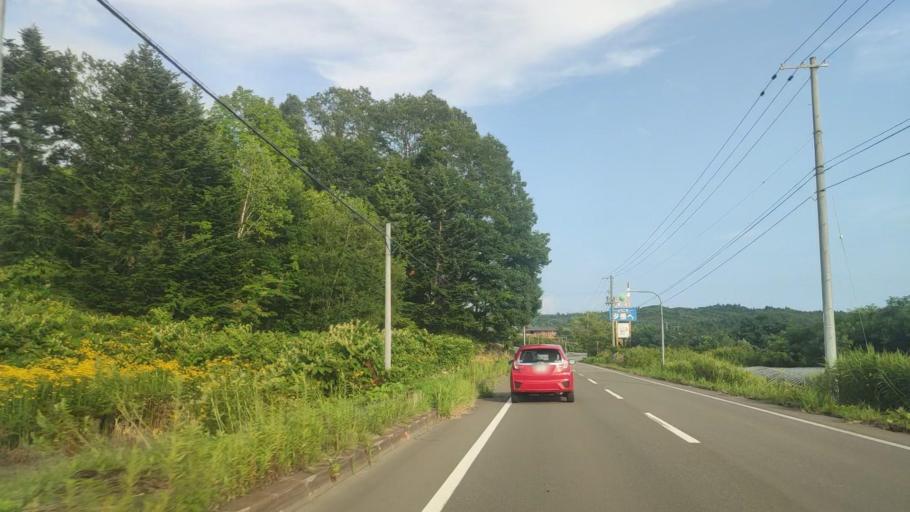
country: JP
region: Hokkaido
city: Iwamizawa
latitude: 43.0411
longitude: 141.9154
